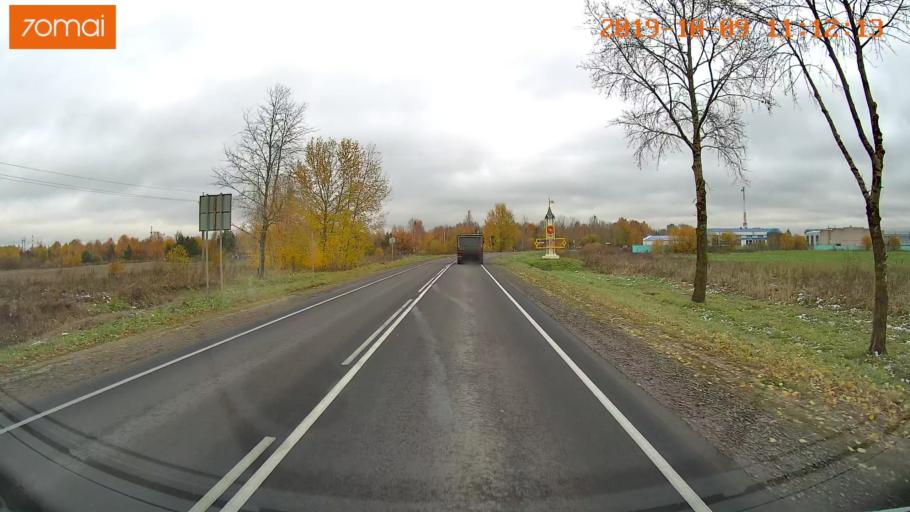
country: RU
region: Vologda
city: Vologda
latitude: 59.1756
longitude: 39.8278
